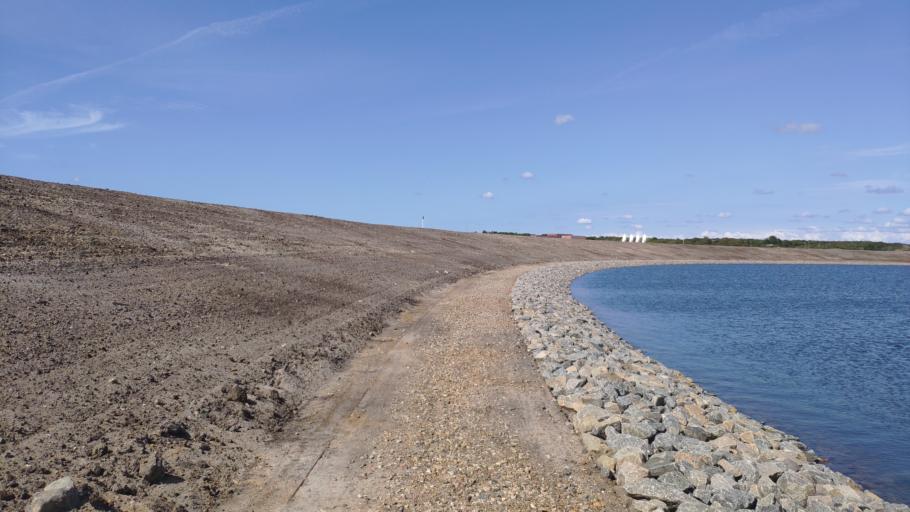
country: DK
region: South Denmark
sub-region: Fano Kommune
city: Nordby
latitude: 55.4825
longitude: 8.4079
